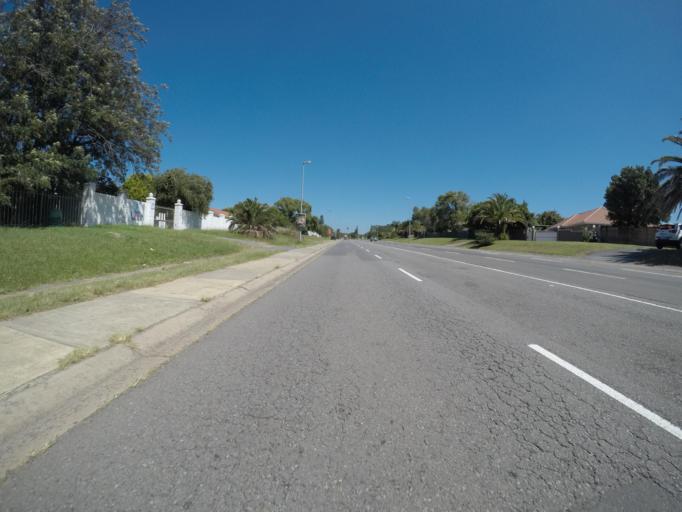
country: ZA
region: Eastern Cape
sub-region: Buffalo City Metropolitan Municipality
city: East London
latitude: -32.9692
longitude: 27.9492
